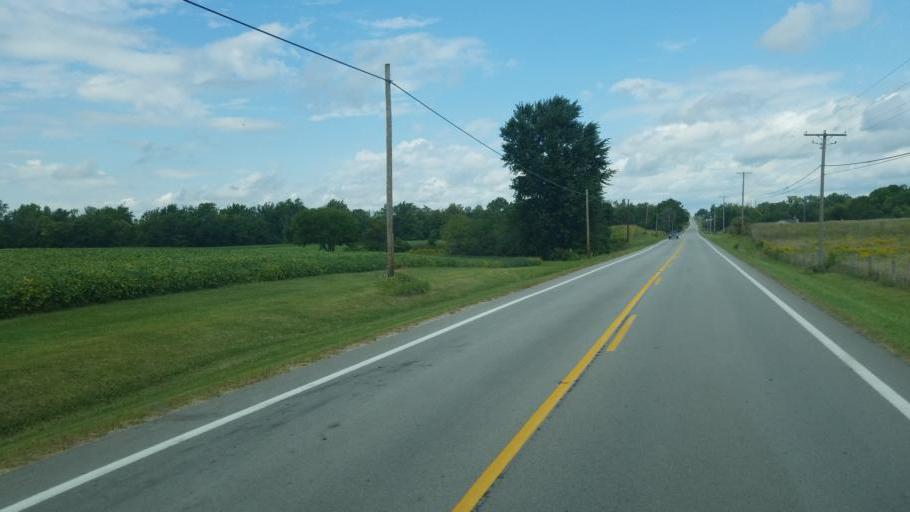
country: US
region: Ohio
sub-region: Seneca County
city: Tiffin
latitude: 41.0596
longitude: -83.0153
